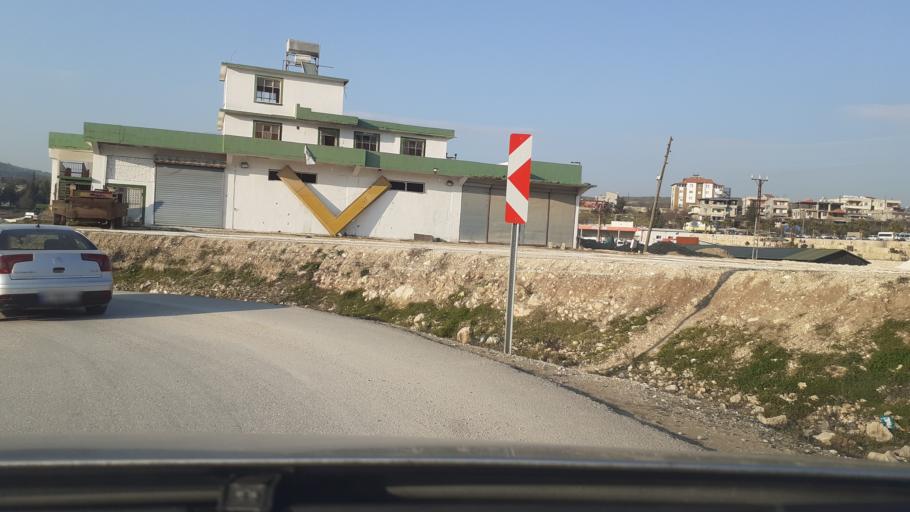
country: TR
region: Hatay
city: Fatikli
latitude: 36.1118
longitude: 36.2635
